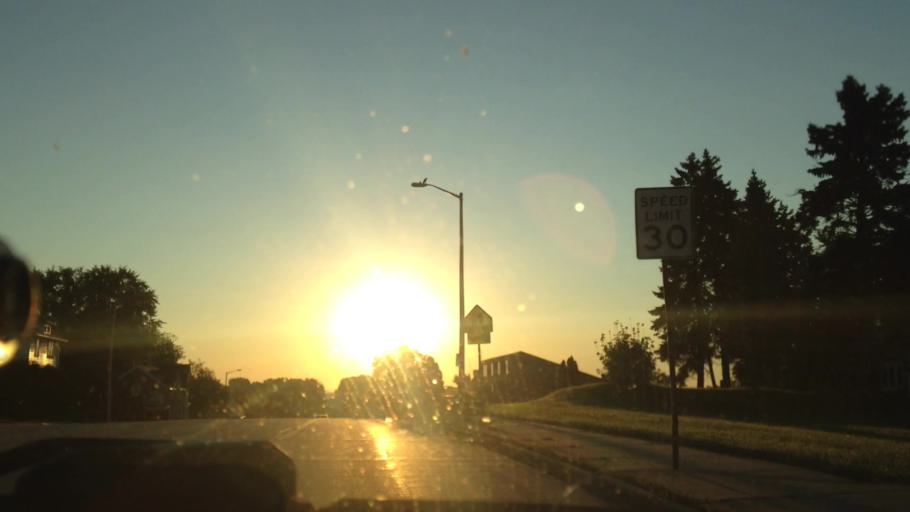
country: US
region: Wisconsin
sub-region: Washington County
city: West Bend
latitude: 43.4268
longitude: -88.1885
